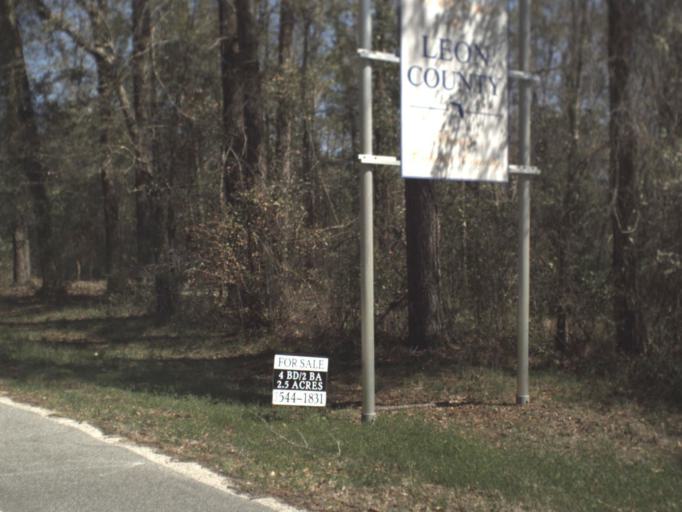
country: US
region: Florida
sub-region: Leon County
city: Woodville
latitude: 30.3035
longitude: -84.3118
